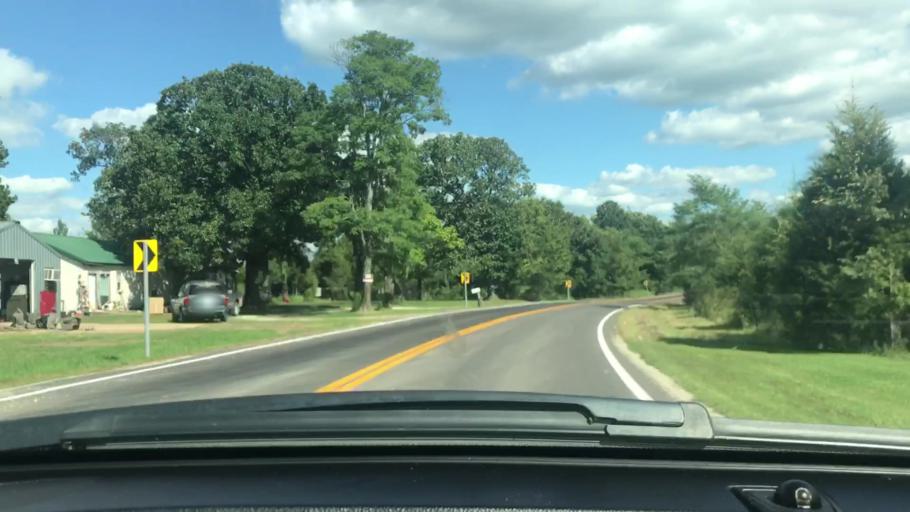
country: US
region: Missouri
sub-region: Wright County
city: Mountain Grove
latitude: 37.2543
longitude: -92.3029
